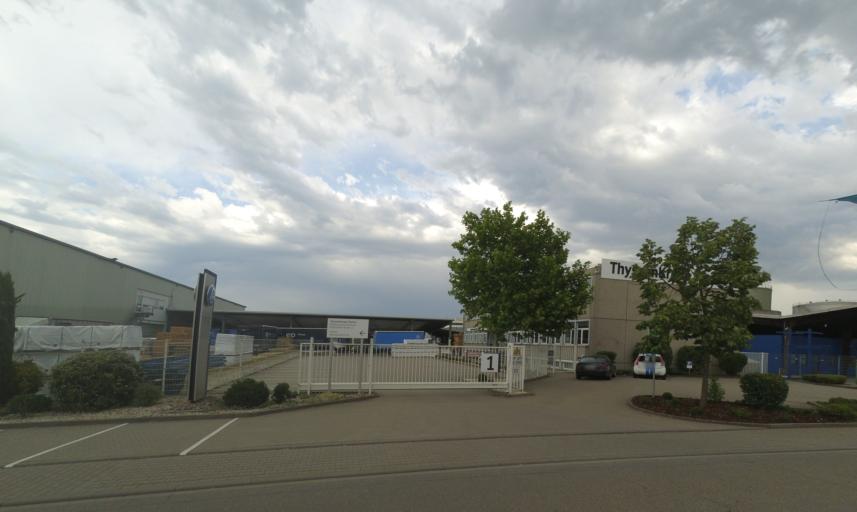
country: DE
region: Rheinland-Pfalz
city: Altrip
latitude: 49.4236
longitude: 8.5145
